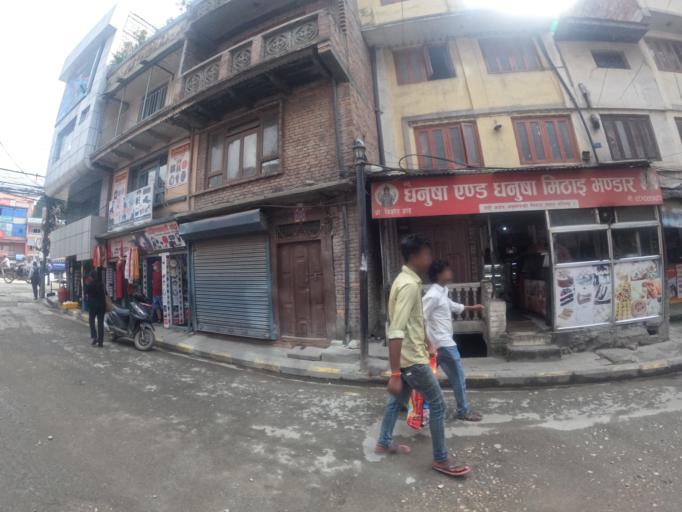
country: NP
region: Central Region
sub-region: Bagmati Zone
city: Bhaktapur
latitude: 27.6729
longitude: 85.3854
